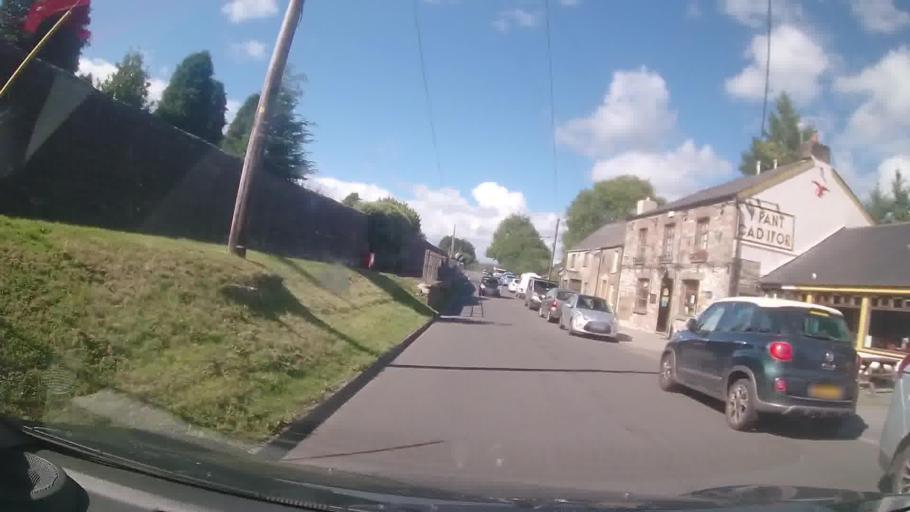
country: GB
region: Wales
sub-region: Merthyr Tydfil County Borough
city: Merthyr Tydfil
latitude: 51.7741
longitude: -3.3613
